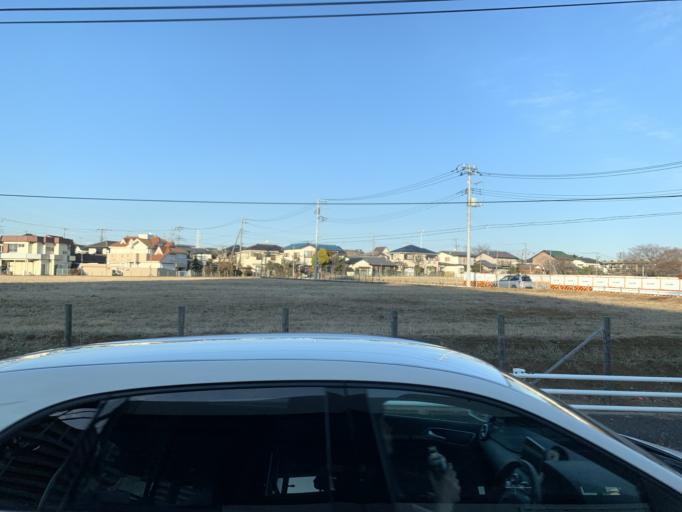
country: JP
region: Chiba
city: Kashiwa
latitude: 35.8670
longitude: 139.9582
